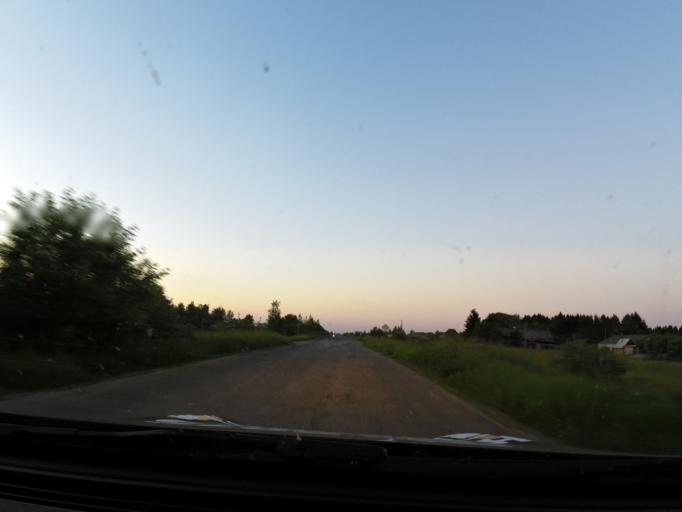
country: RU
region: Kostroma
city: Buy
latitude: 58.4631
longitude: 41.4074
